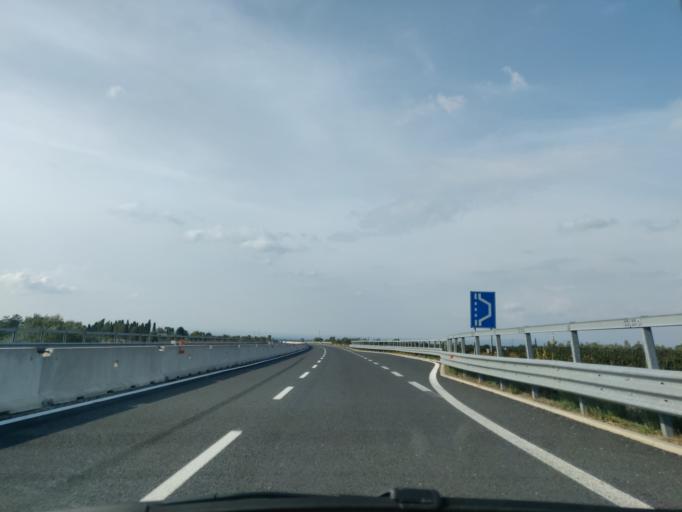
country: IT
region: Latium
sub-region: Provincia di Viterbo
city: Blera
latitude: 42.3214
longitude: 11.9902
